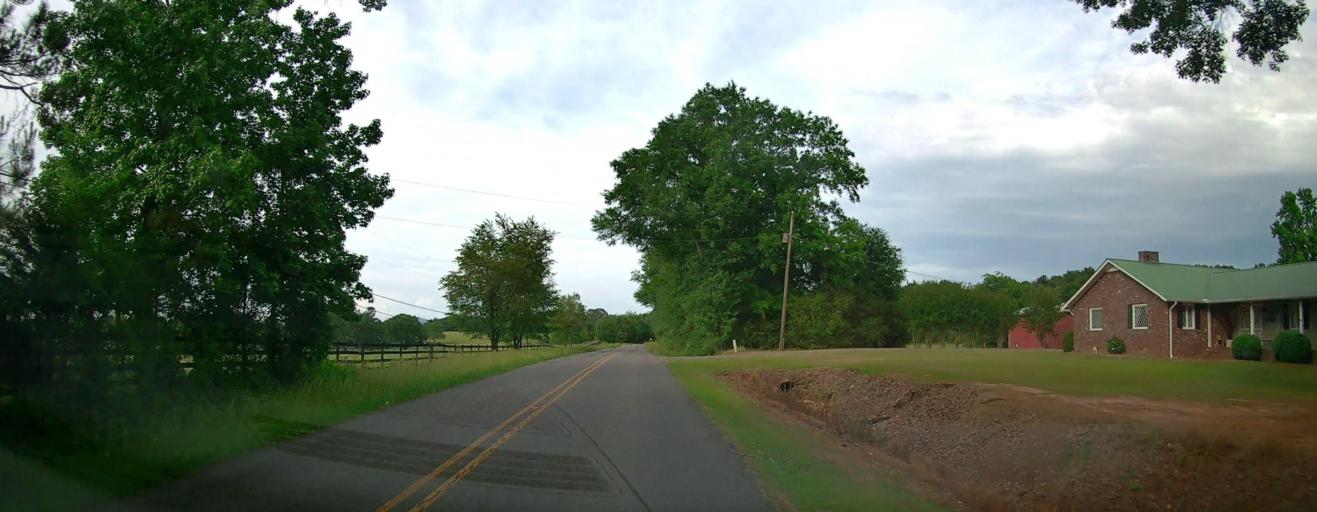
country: US
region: Alabama
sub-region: Calhoun County
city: Oxford
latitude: 33.5778
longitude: -85.8352
